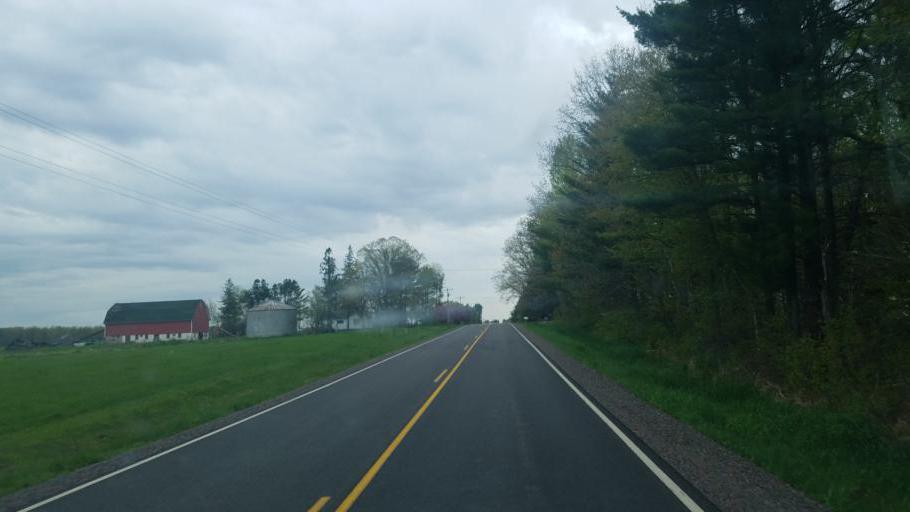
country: US
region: Wisconsin
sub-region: Wood County
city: Marshfield
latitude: 44.4790
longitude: -90.2800
